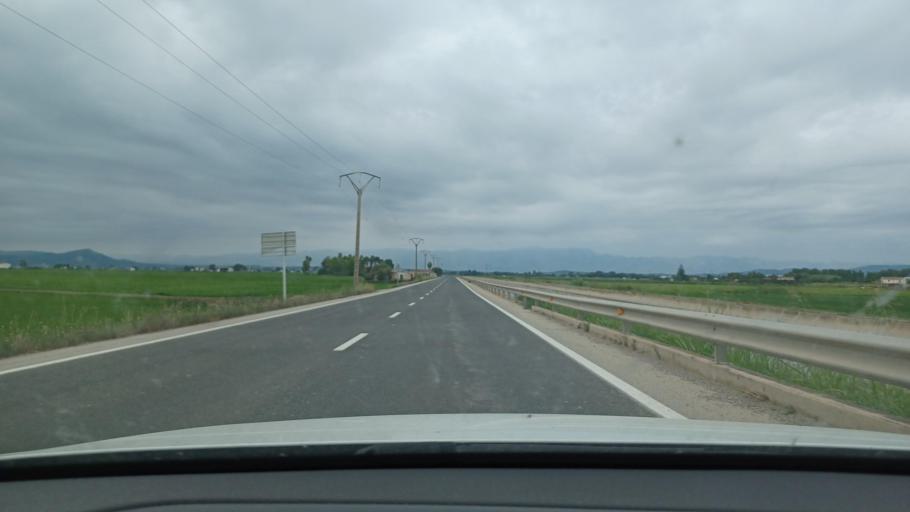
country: ES
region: Catalonia
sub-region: Provincia de Tarragona
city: Deltebre
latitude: 40.7098
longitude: 0.6838
